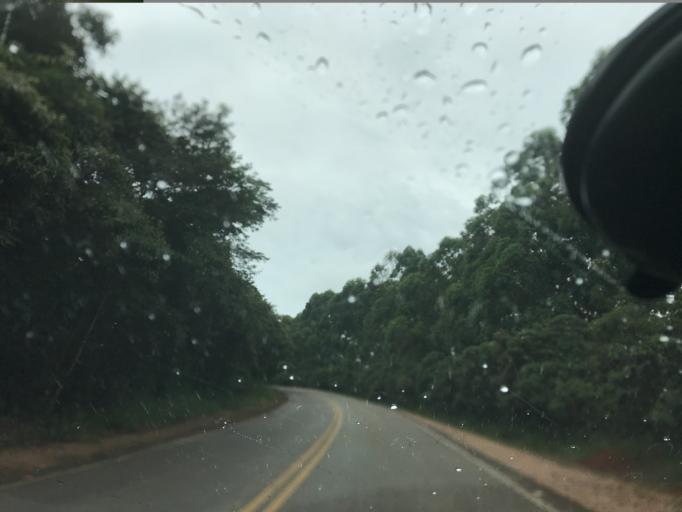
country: BR
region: Minas Gerais
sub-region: Conceicao Do Rio Verde
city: Conceicao do Rio Verde
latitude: -21.6874
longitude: -45.0151
